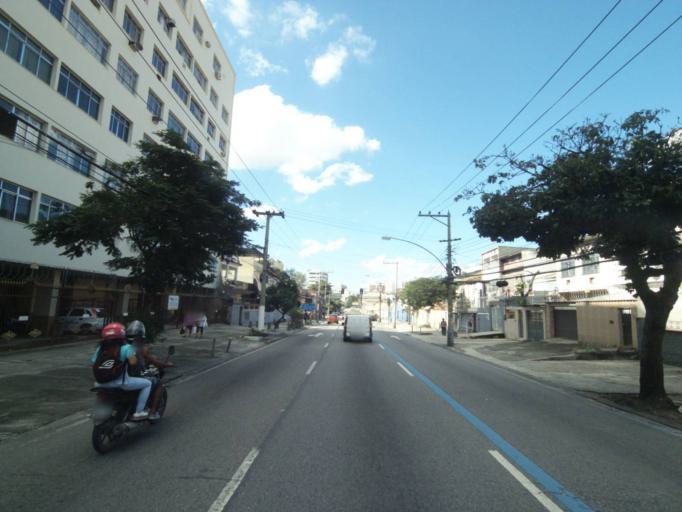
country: BR
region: Rio de Janeiro
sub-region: Rio De Janeiro
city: Rio de Janeiro
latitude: -22.9036
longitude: -43.2567
